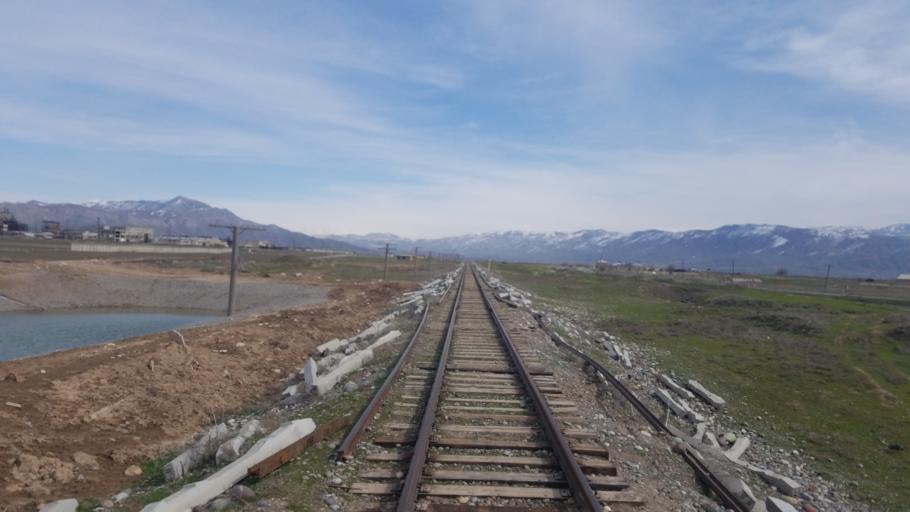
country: TJ
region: Khatlon
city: Yovon
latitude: 38.2819
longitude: 68.9301
